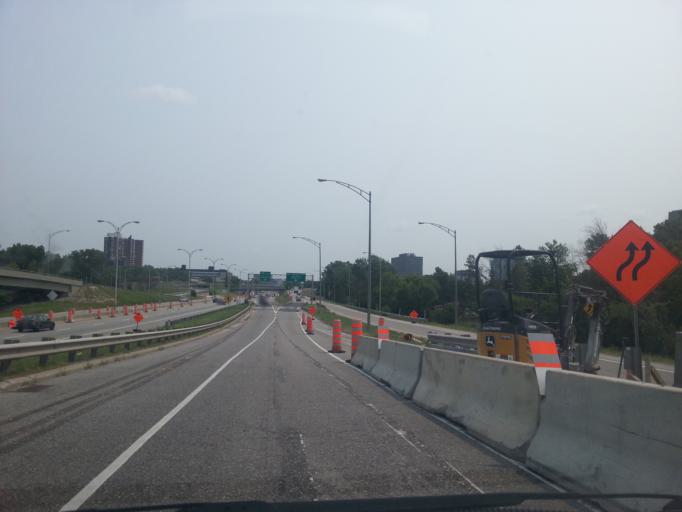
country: CA
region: Ontario
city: Ottawa
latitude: 45.4402
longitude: -75.7180
